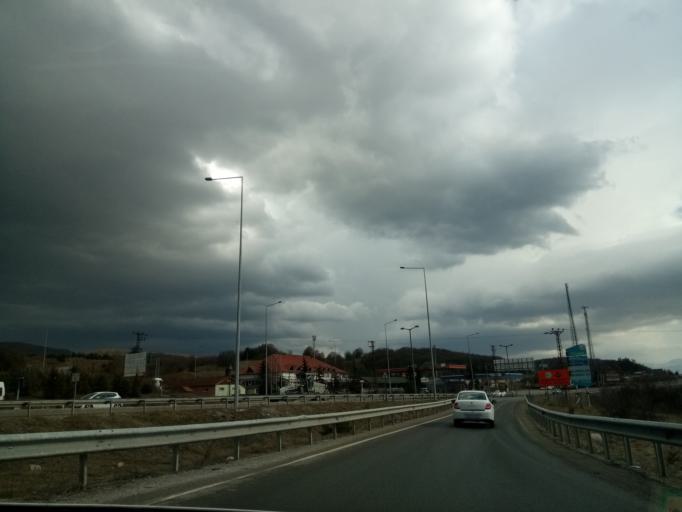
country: TR
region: Bolu
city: Bolu
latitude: 40.7141
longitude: 31.4767
